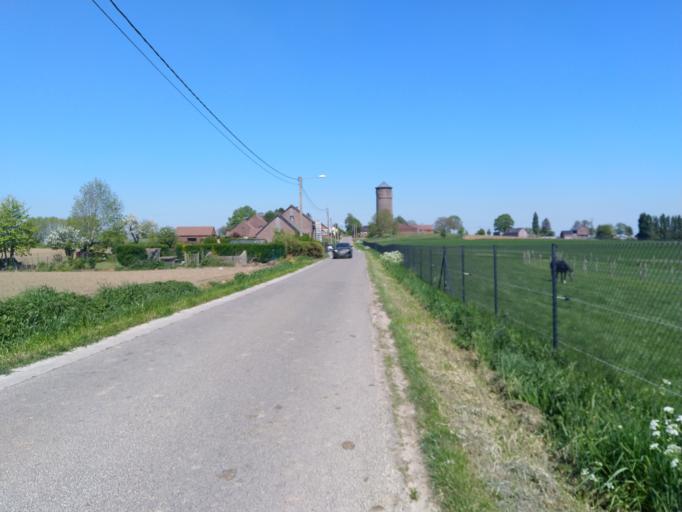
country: BE
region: Wallonia
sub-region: Province du Hainaut
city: Enghien
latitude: 50.6283
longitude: 4.0174
